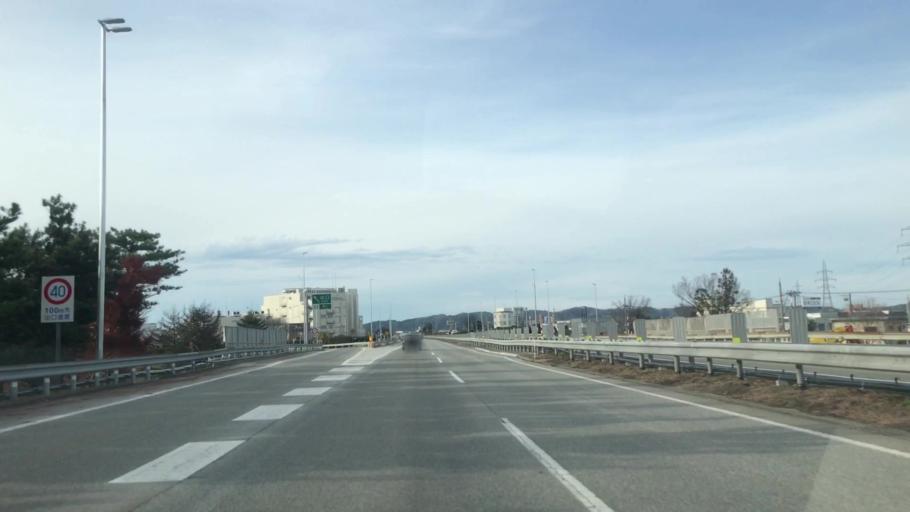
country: JP
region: Toyama
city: Toyama-shi
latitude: 36.6548
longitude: 137.2064
